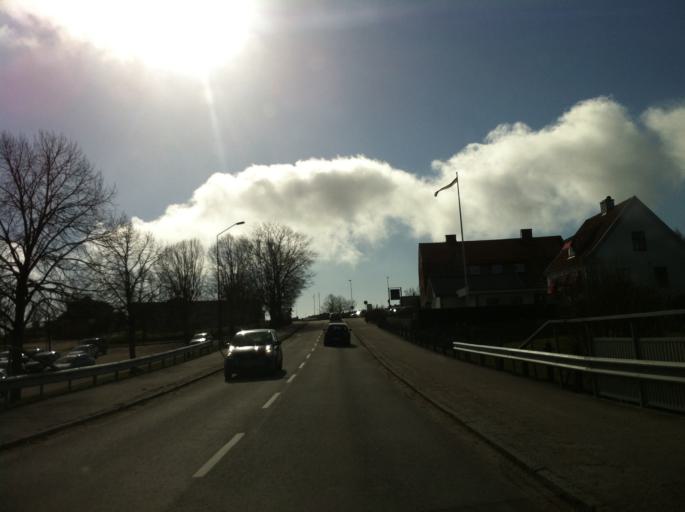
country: SE
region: Skane
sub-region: Bastads Kommun
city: Forslov
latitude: 56.3502
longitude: 12.8177
